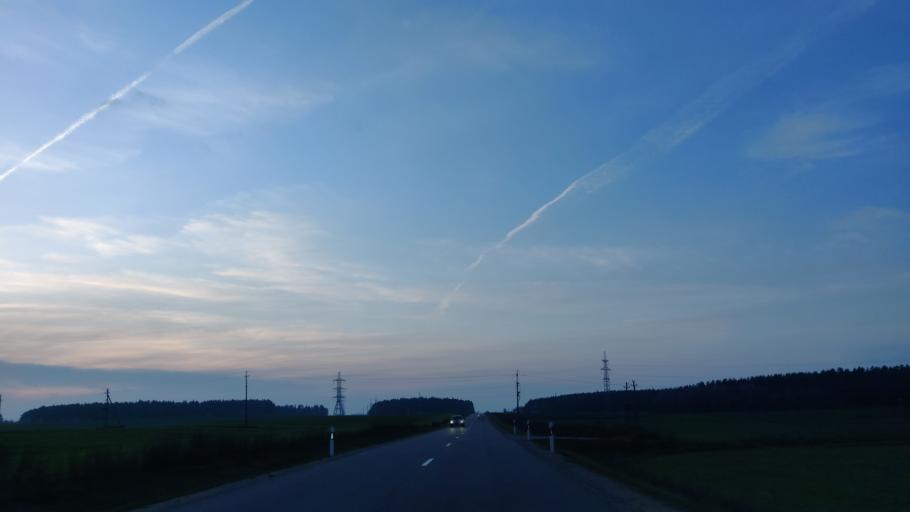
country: LT
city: Lentvaris
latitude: 54.5940
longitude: 25.0418
